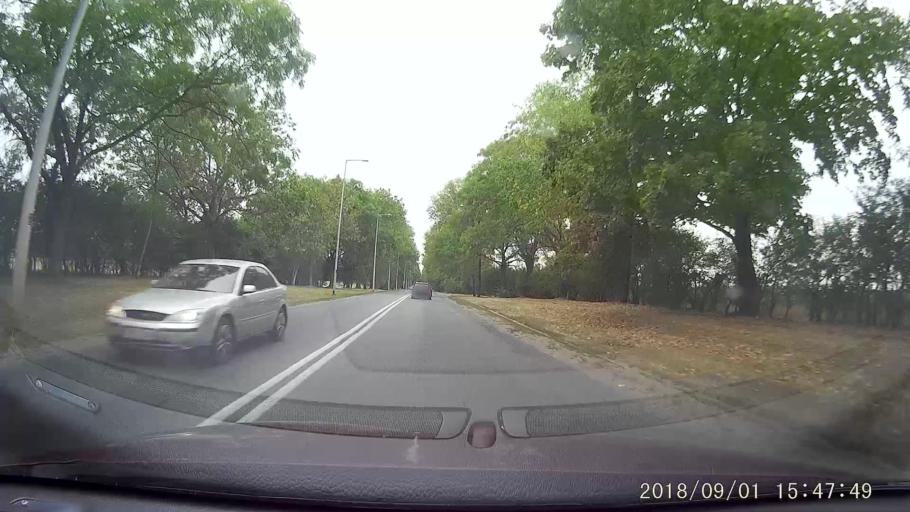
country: PL
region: Lubusz
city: Gorzow Wielkopolski
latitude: 52.7408
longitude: 15.1858
